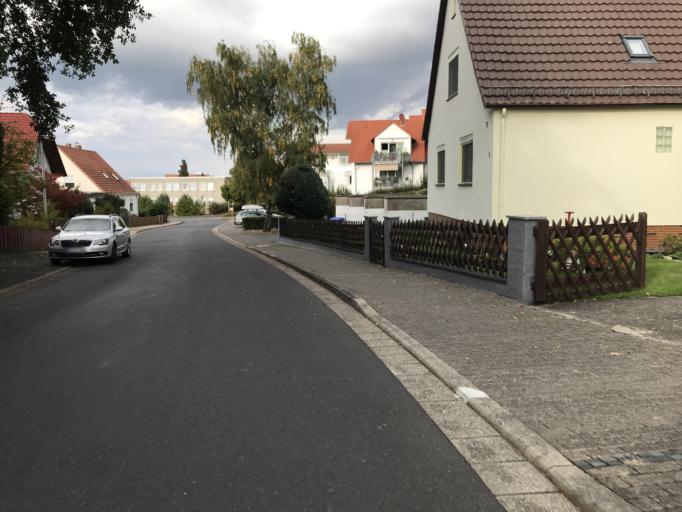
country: DE
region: Hesse
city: Borken
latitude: 51.0432
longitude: 9.2799
